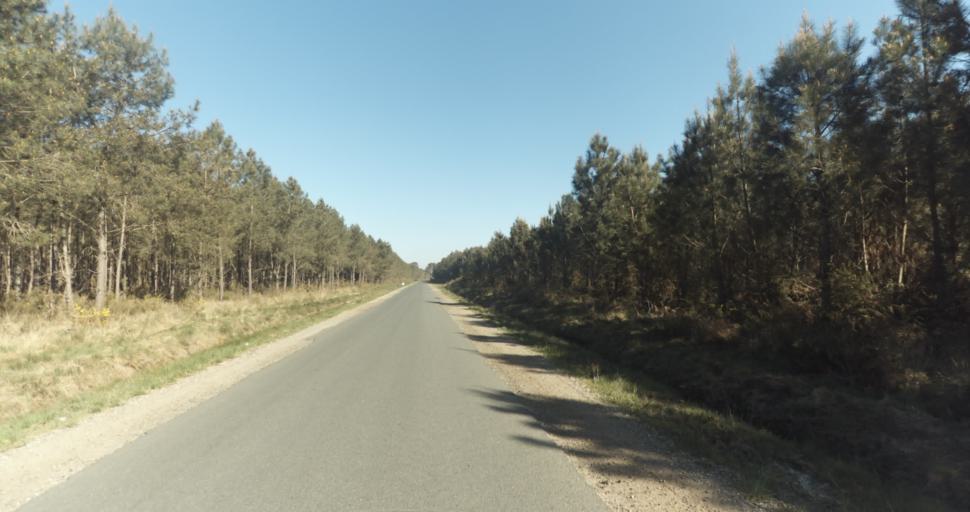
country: FR
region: Aquitaine
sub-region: Departement de la Gironde
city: Marcheprime
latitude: 44.7526
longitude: -0.8488
